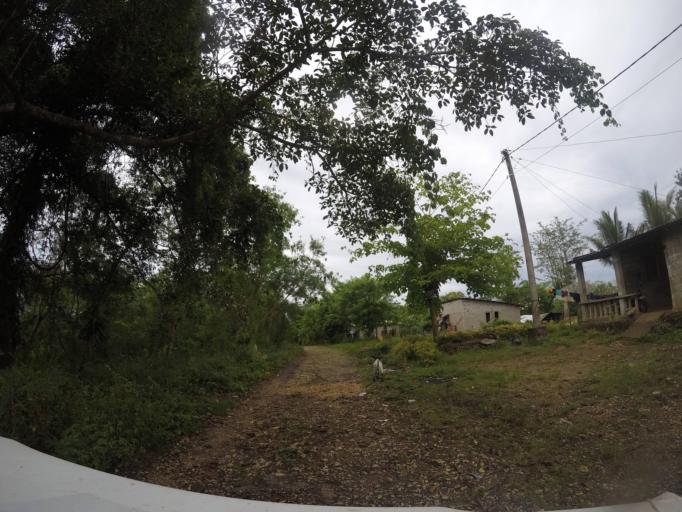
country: TL
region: Lautem
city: Lospalos
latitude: -8.5308
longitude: 127.0031
